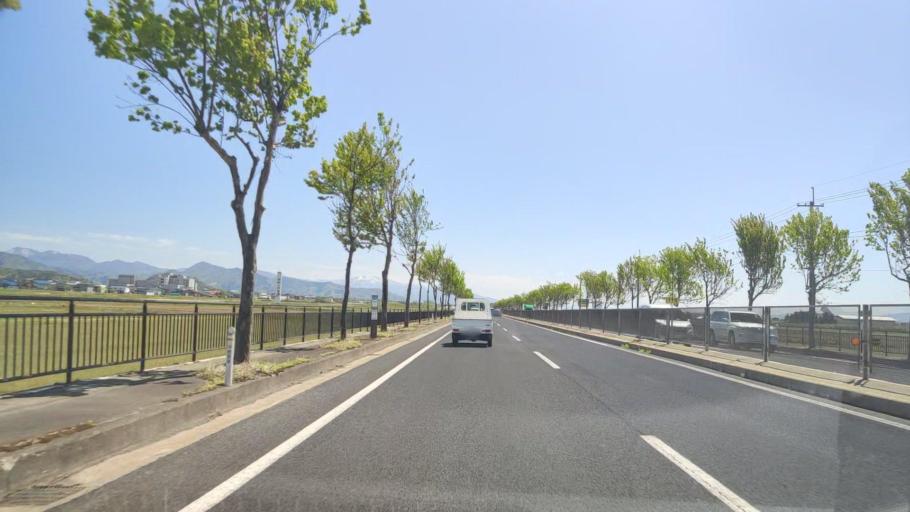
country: JP
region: Yamagata
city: Higashine
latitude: 38.4705
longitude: 140.3828
